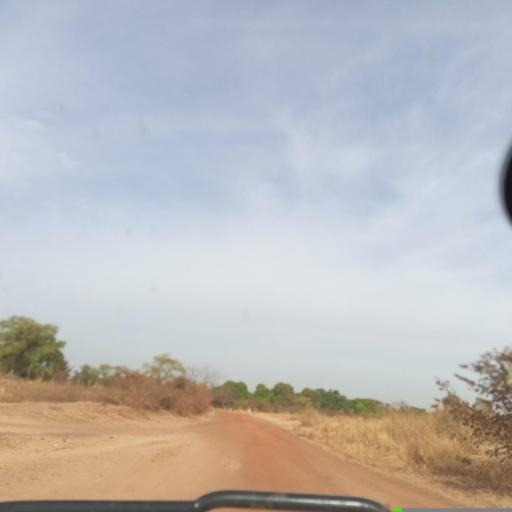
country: ML
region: Koulikoro
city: Koulikoro
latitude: 13.1075
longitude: -7.6475
